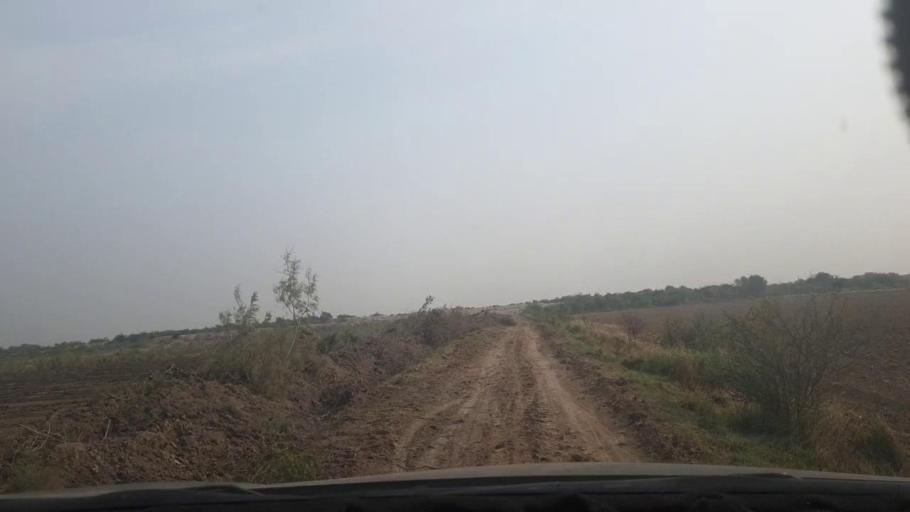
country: PK
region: Sindh
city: Jamshoro
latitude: 25.5197
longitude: 68.3217
